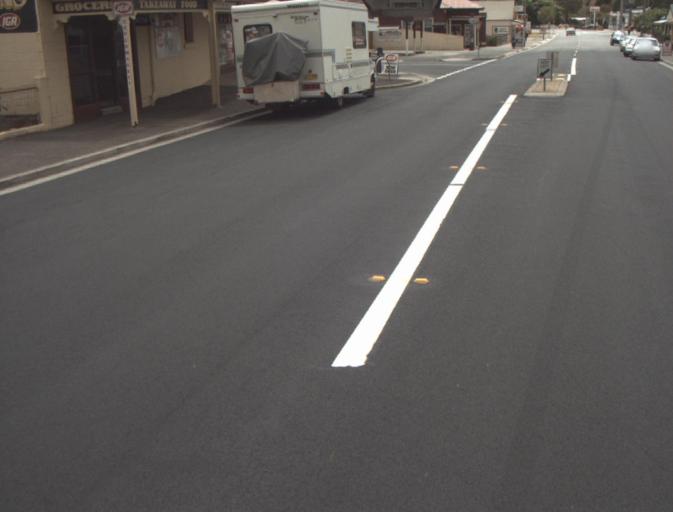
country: AU
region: Tasmania
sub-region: Launceston
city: Mayfield
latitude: -41.2508
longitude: 147.2170
